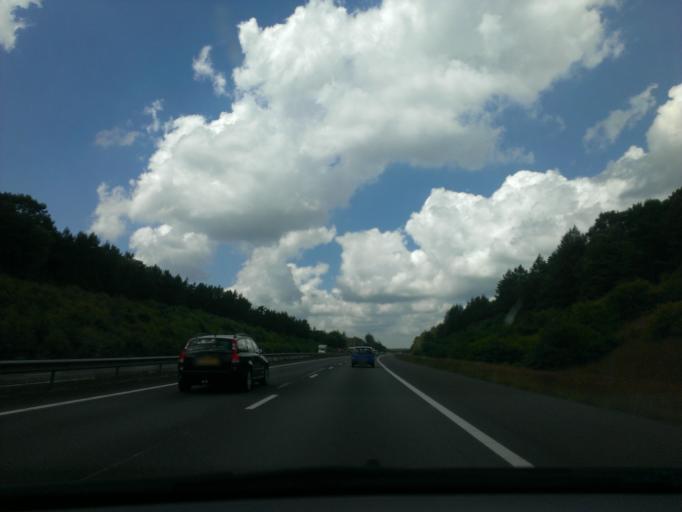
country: NL
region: Gelderland
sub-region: Gemeente Apeldoorn
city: Uddel
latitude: 52.1924
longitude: 5.8413
